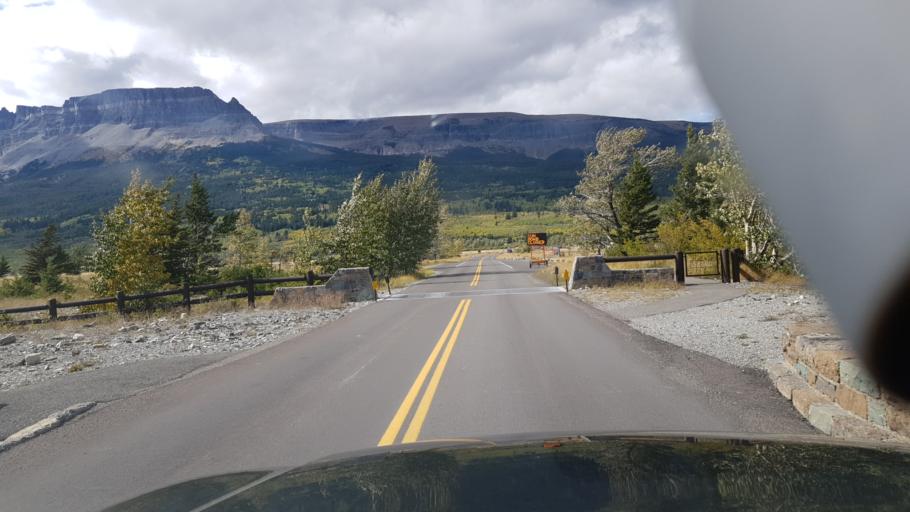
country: US
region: Montana
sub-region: Glacier County
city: North Browning
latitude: 48.7441
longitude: -113.4312
